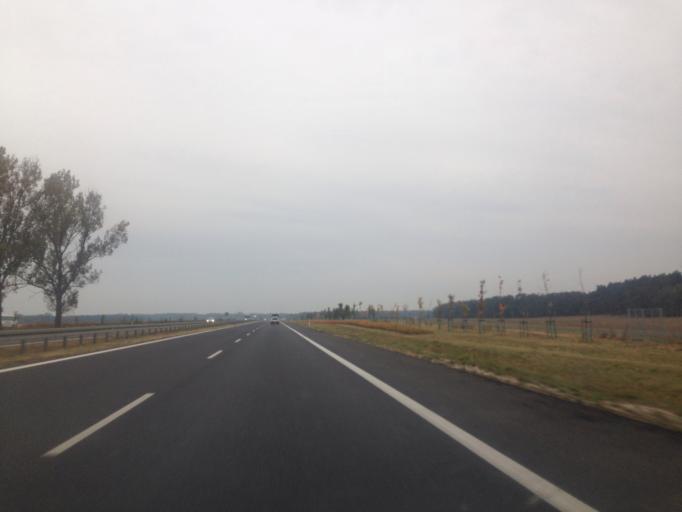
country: PL
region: Greater Poland Voivodeship
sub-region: Powiat poznanski
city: Pobiedziska
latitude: 52.4219
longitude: 17.3028
